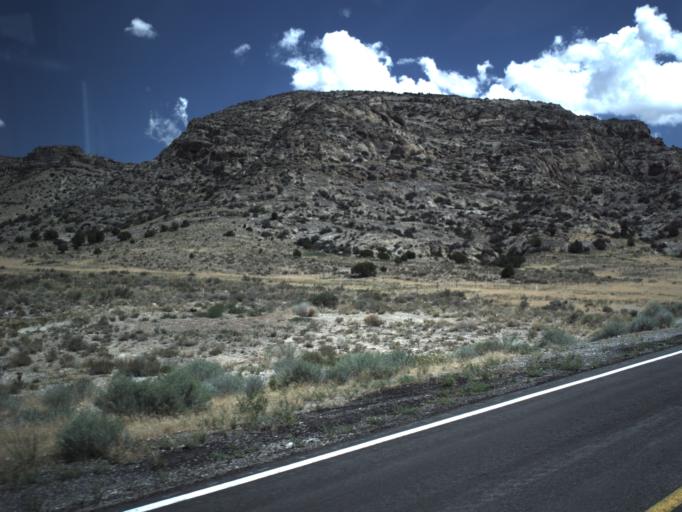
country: US
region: Utah
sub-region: Beaver County
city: Milford
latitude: 39.0721
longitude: -113.6607
